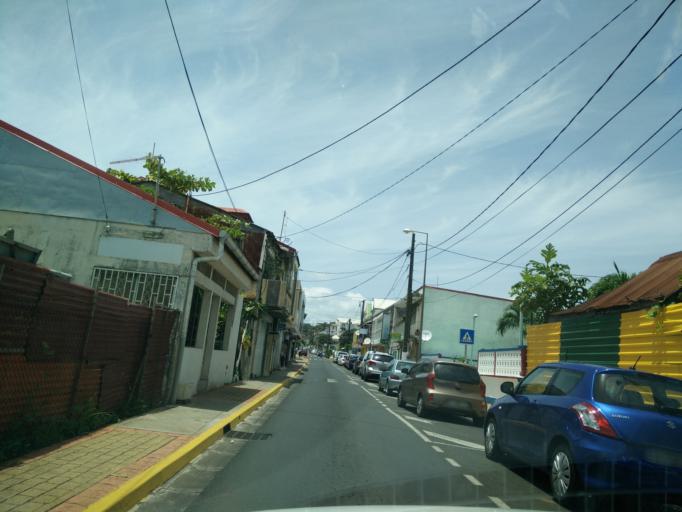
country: GP
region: Guadeloupe
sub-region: Guadeloupe
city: Petit-Bourg
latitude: 16.1933
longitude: -61.5908
